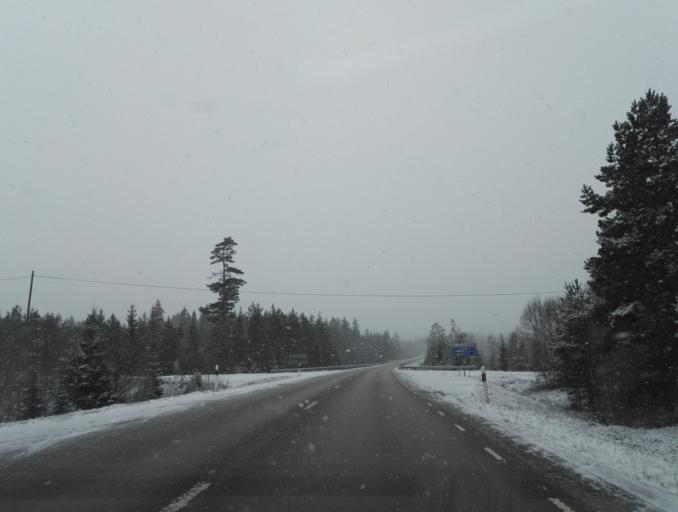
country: SE
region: Kronoberg
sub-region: Uppvidinge Kommun
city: Lenhovda
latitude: 57.0986
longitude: 15.2029
